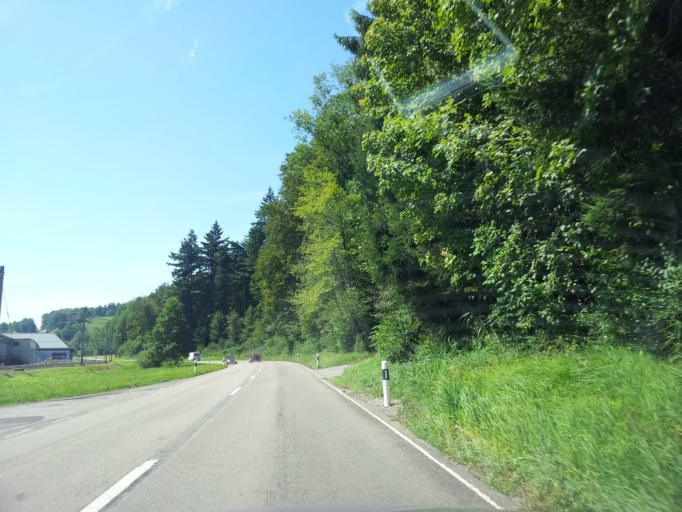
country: CH
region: Saint Gallen
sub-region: Wahlkreis See-Gaster
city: Eschenbach
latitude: 47.2262
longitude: 8.9200
